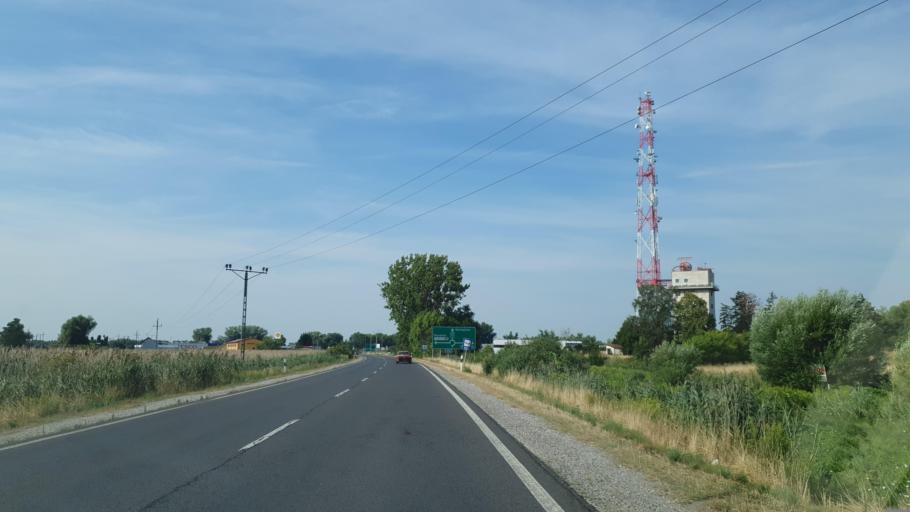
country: HU
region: Szabolcs-Szatmar-Bereg
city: Doge
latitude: 48.2369
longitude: 22.0663
